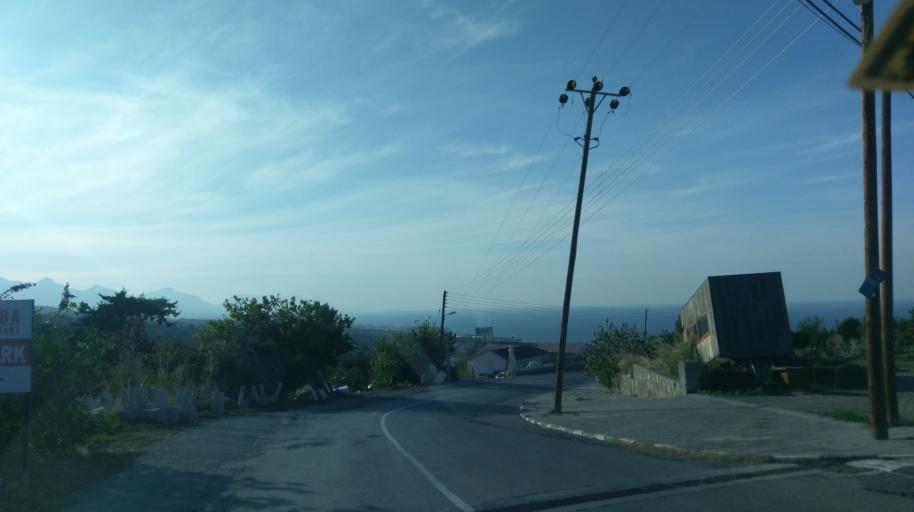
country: CY
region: Ammochostos
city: Lefkonoiko
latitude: 35.3402
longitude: 33.5791
